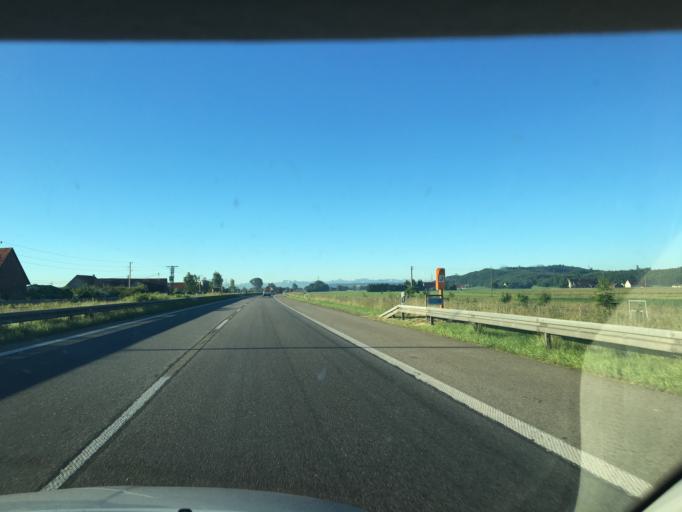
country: DE
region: Bavaria
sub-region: Swabia
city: Benningen
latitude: 47.9530
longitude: 10.1929
